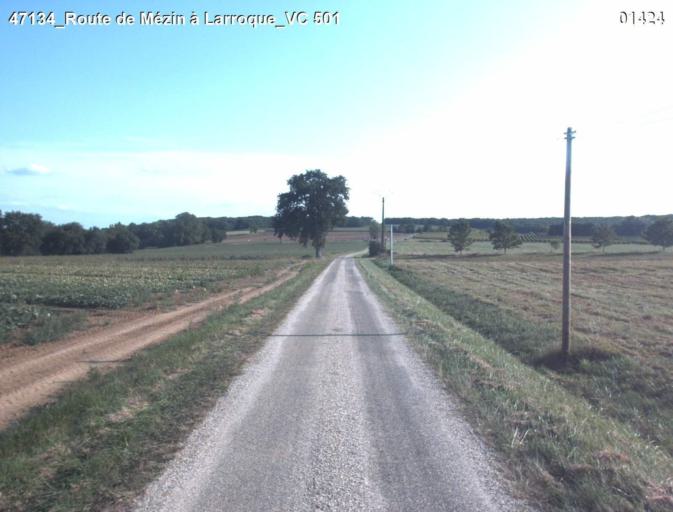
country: FR
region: Aquitaine
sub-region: Departement du Lot-et-Garonne
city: Mezin
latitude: 44.0106
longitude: 0.2762
